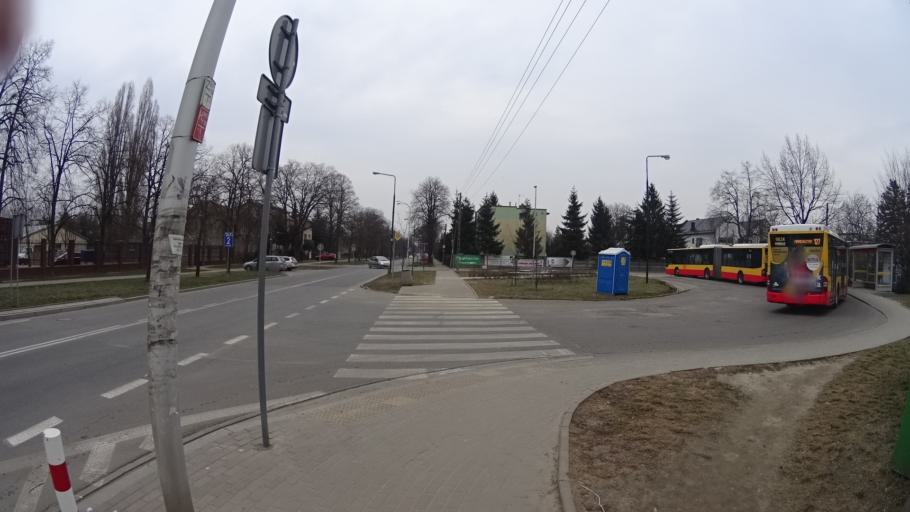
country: PL
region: Masovian Voivodeship
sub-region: Warszawa
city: Ursus
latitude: 52.2091
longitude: 20.8948
